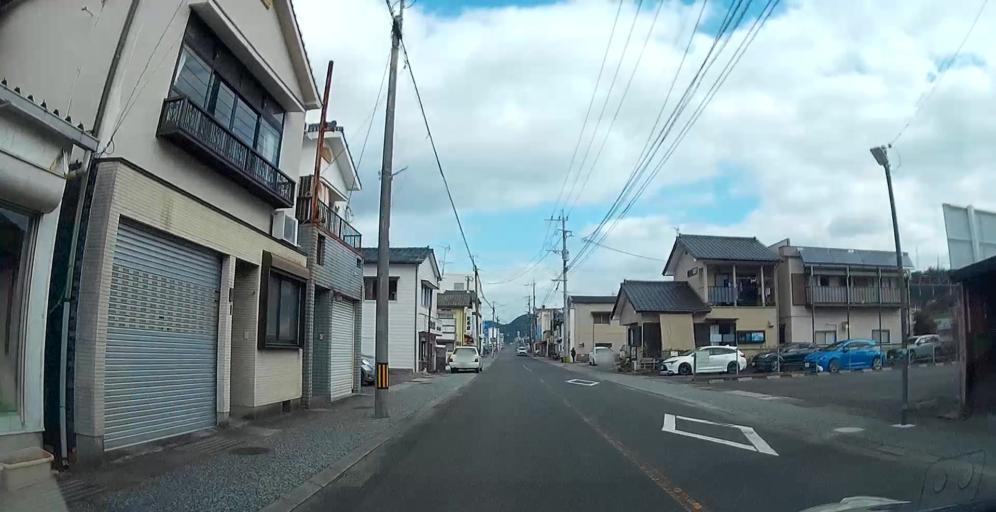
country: JP
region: Kumamoto
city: Minamata
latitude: 32.2040
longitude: 130.3940
